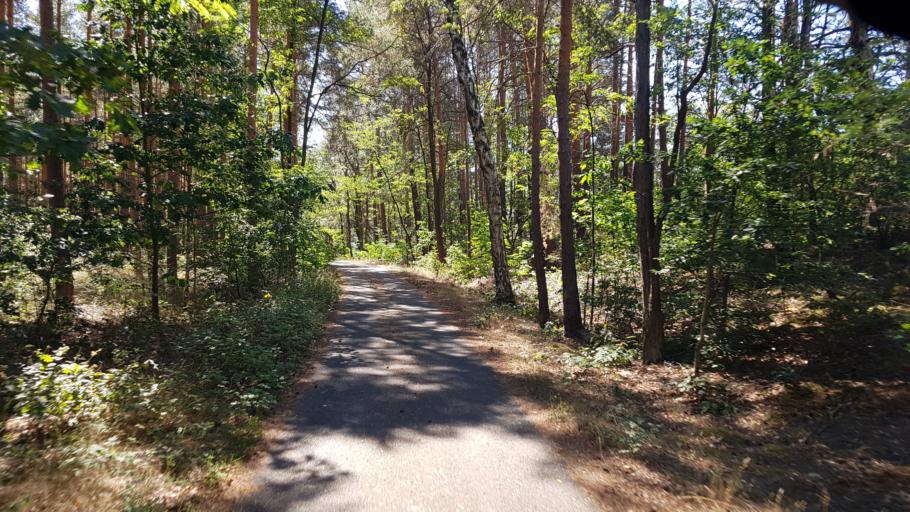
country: DE
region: Brandenburg
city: Calau
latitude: 51.7030
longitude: 13.9995
